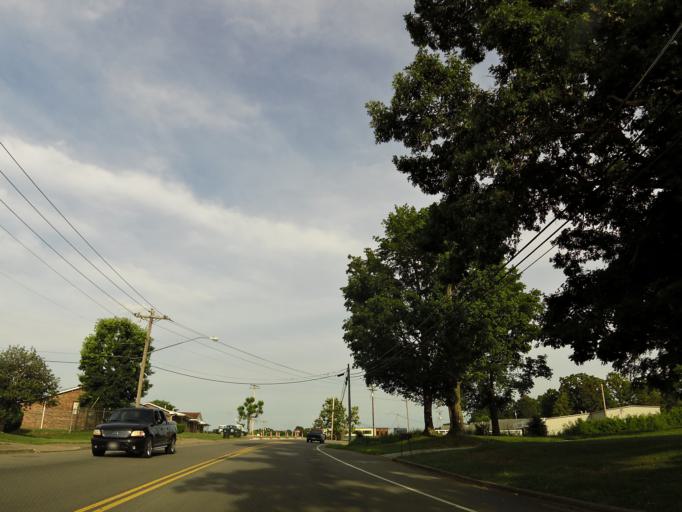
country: US
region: Tennessee
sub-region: Dickson County
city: Dickson
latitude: 36.0677
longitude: -87.3776
